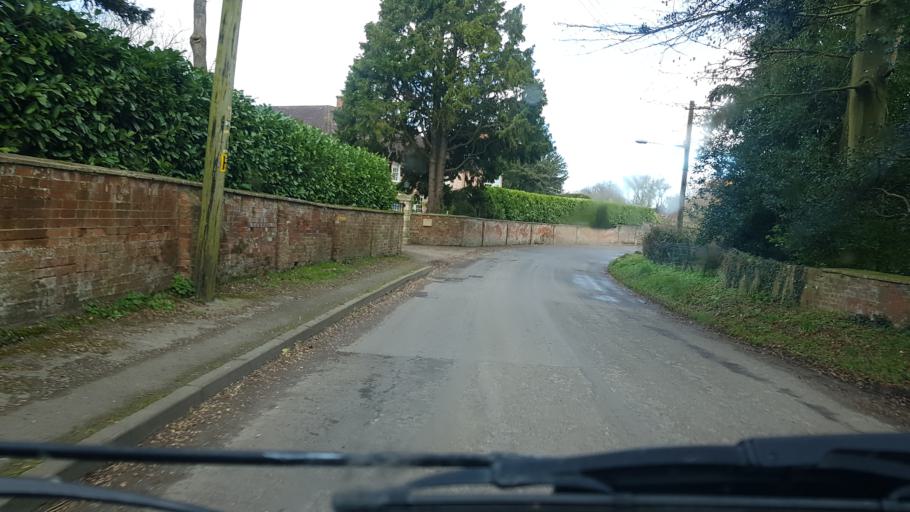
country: GB
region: England
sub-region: Wiltshire
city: Wilsford
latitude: 51.3177
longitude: -1.8799
